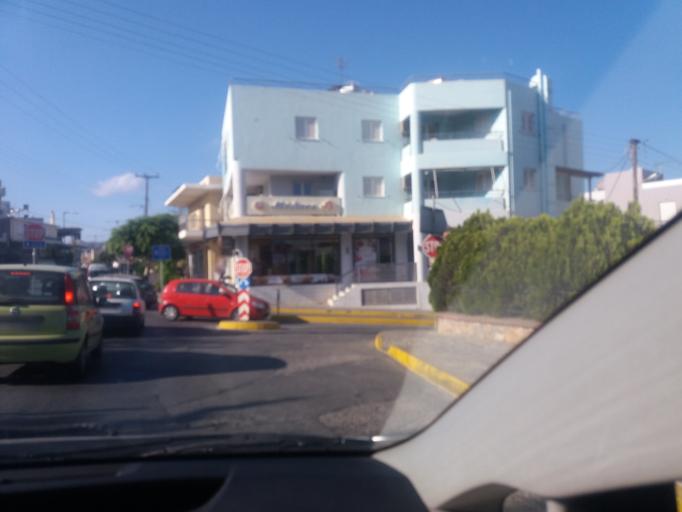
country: GR
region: Crete
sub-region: Nomos Lasithiou
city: Agios Nikolaos
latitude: 35.1948
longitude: 25.7135
